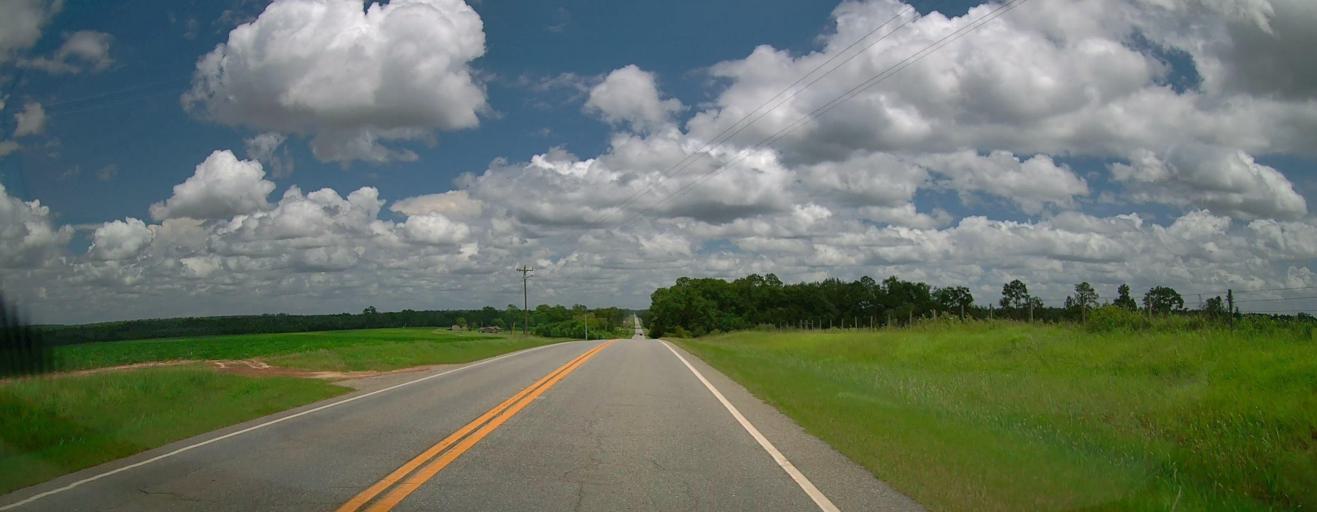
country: US
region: Georgia
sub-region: Turner County
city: Ashburn
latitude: 31.7217
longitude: -83.5165
